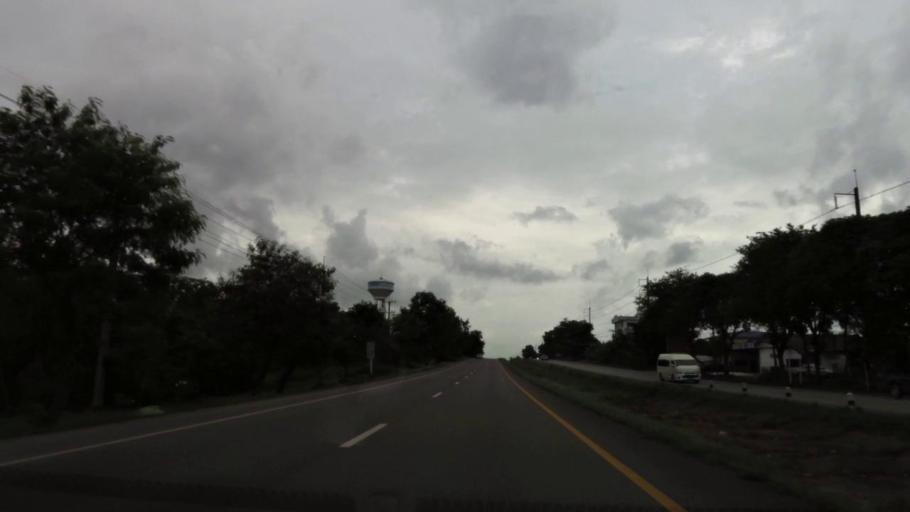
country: TH
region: Chanthaburi
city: Tha Mai
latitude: 12.7024
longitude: 101.9854
